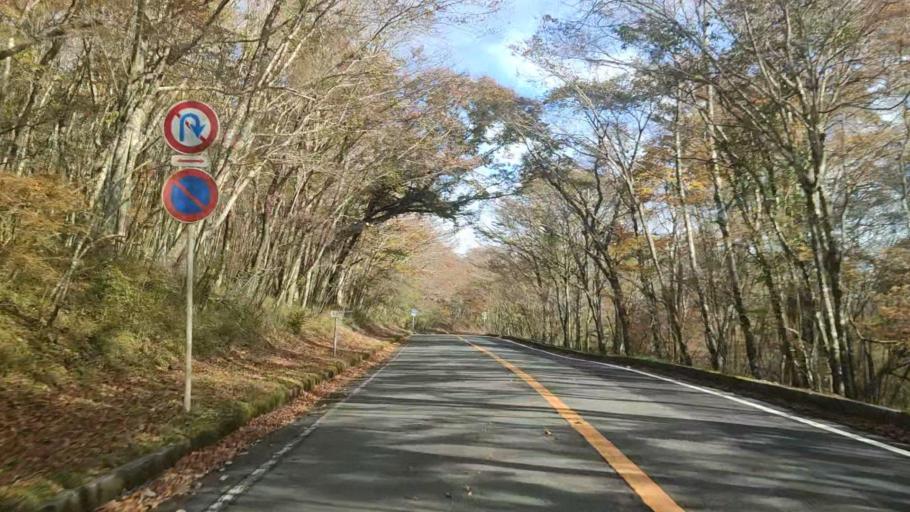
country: JP
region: Shizuoka
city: Fujinomiya
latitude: 35.2966
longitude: 138.7033
